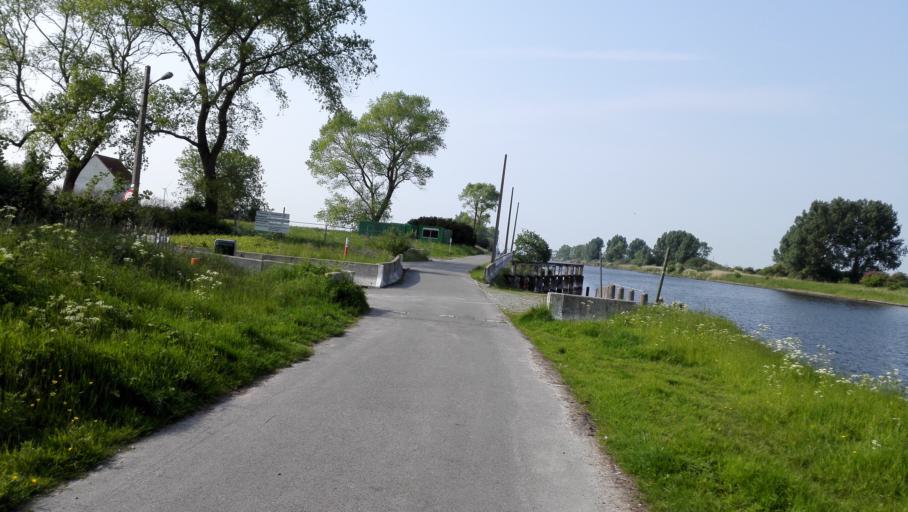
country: BE
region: Flanders
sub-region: Provincie West-Vlaanderen
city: Zeebrugge
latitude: 51.2937
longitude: 3.2063
